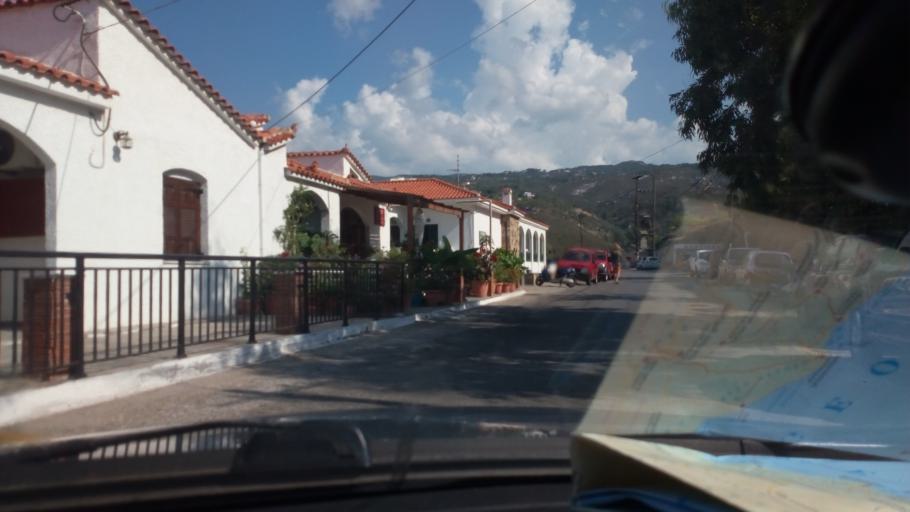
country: GR
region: North Aegean
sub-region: Nomos Samou
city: Agios Kirykos
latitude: 37.6328
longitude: 26.0891
